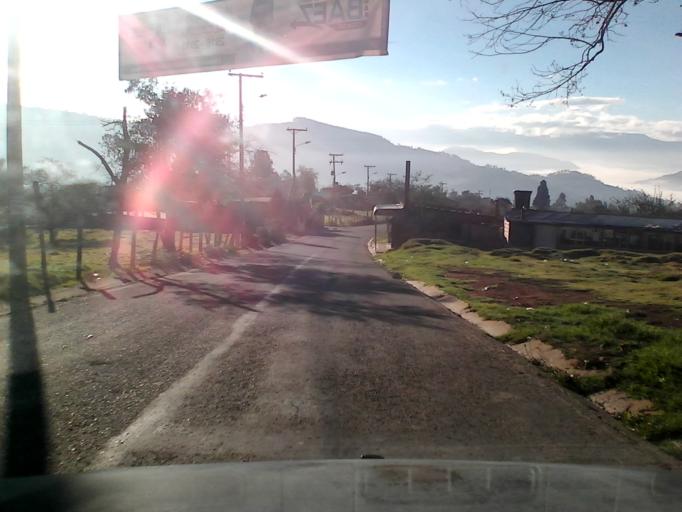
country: CO
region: Boyaca
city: Duitama
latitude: 5.8553
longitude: -73.0369
